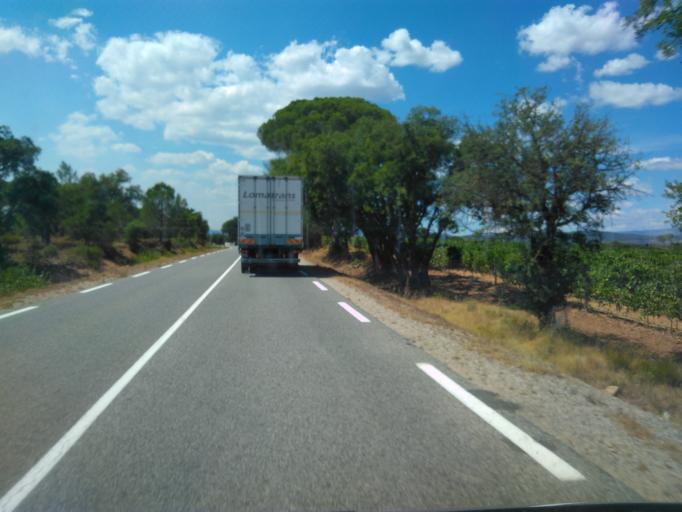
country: FR
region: Provence-Alpes-Cote d'Azur
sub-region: Departement du Var
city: Le Cannet-des-Maures
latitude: 43.3570
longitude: 6.4062
